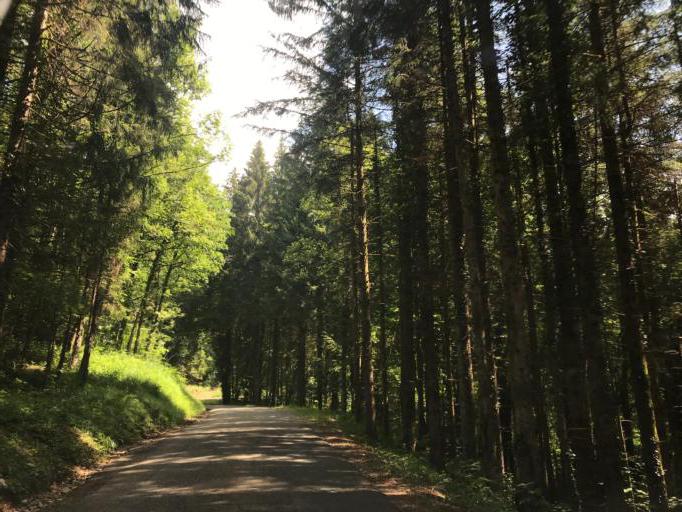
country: FR
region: Franche-Comte
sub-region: Departement du Jura
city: Moirans-en-Montagne
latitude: 46.4940
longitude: 5.7618
